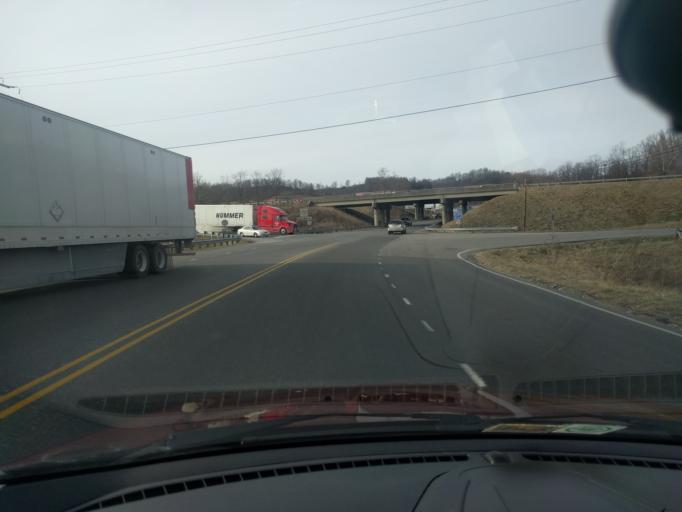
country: US
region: Virginia
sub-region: Augusta County
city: Stuarts Draft
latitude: 37.9310
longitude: -79.2277
